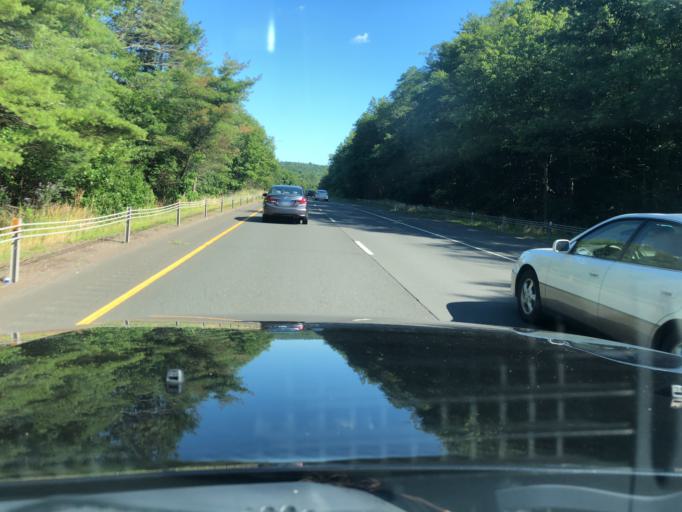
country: US
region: Connecticut
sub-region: Middlesex County
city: Higganum
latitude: 41.4864
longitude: -72.5644
